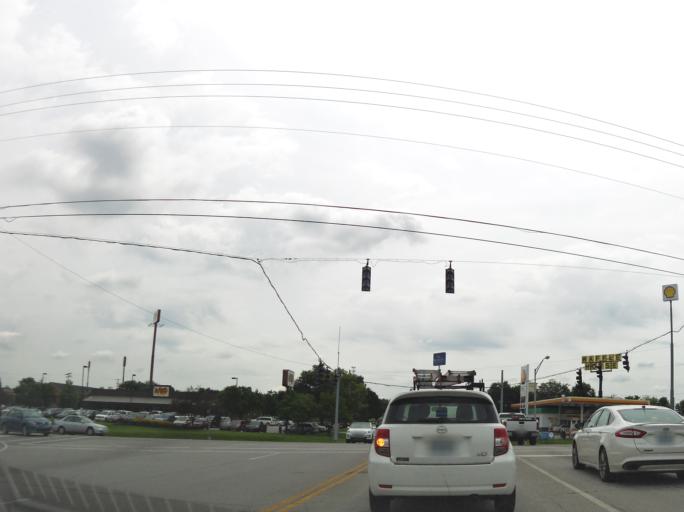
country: US
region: Kentucky
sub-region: Scott County
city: Georgetown
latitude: 38.2206
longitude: -84.5414
